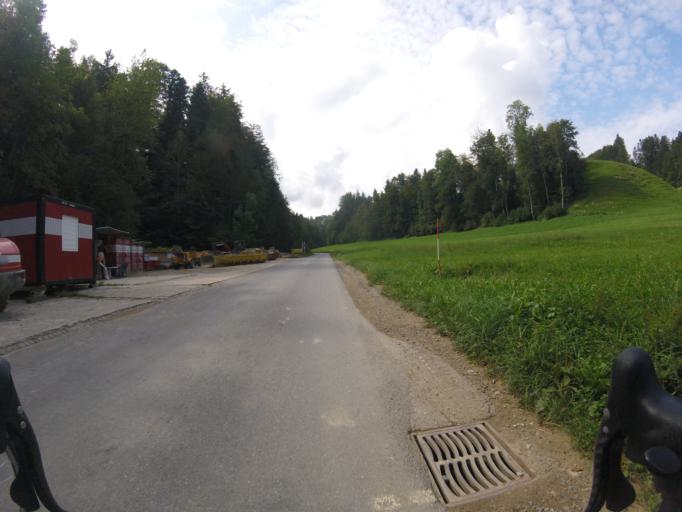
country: CH
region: Bern
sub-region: Emmental District
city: Oberburg
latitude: 47.0279
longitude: 7.6063
